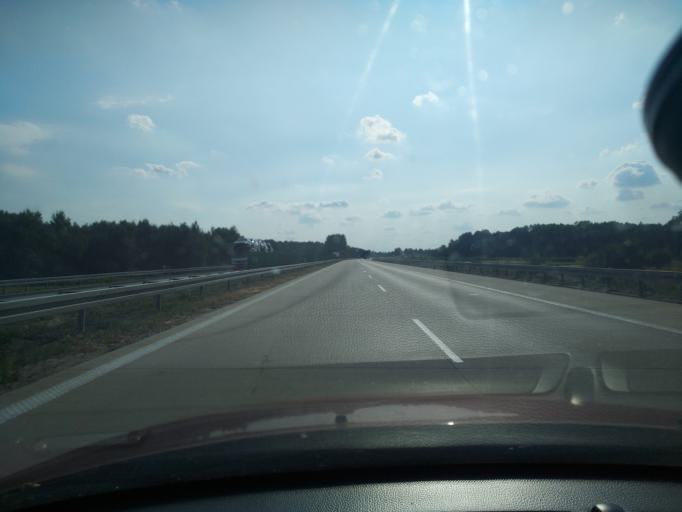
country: PL
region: Lower Silesian Voivodeship
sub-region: Powiat zgorzelecki
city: Lagow
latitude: 51.1739
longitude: 15.0780
